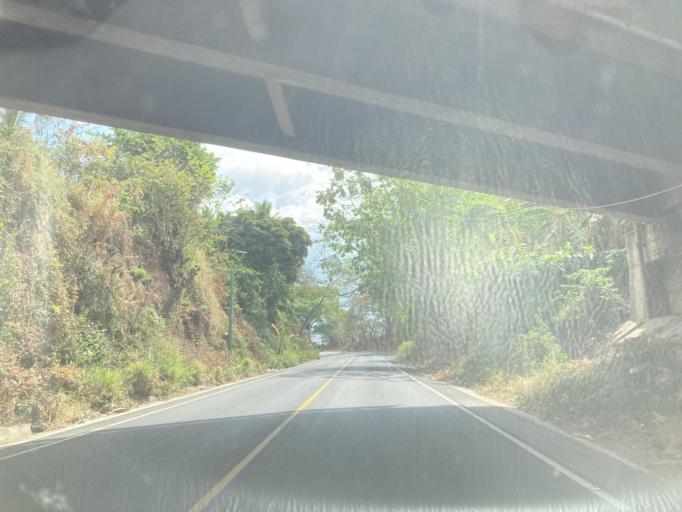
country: GT
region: Santa Rosa
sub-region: Municipio de Taxisco
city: Taxisco
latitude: 14.0633
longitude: -90.4676
